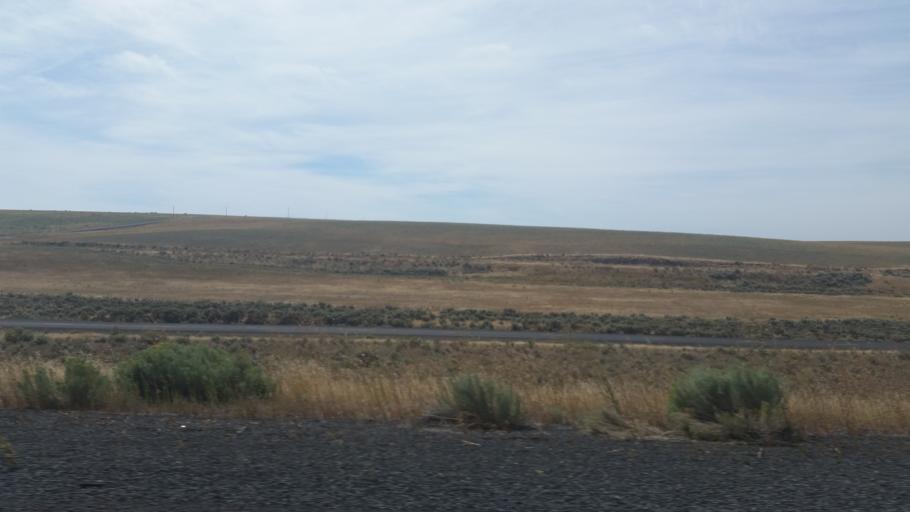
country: US
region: Washington
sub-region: Adams County
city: Ritzville
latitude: 47.1004
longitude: -118.6055
